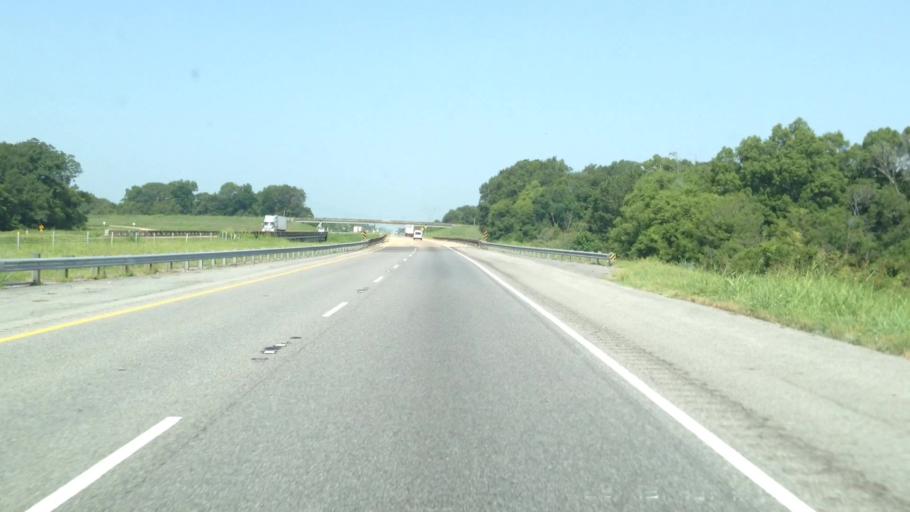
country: US
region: Louisiana
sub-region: Madison Parish
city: Tallulah
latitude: 32.4191
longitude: -91.2957
